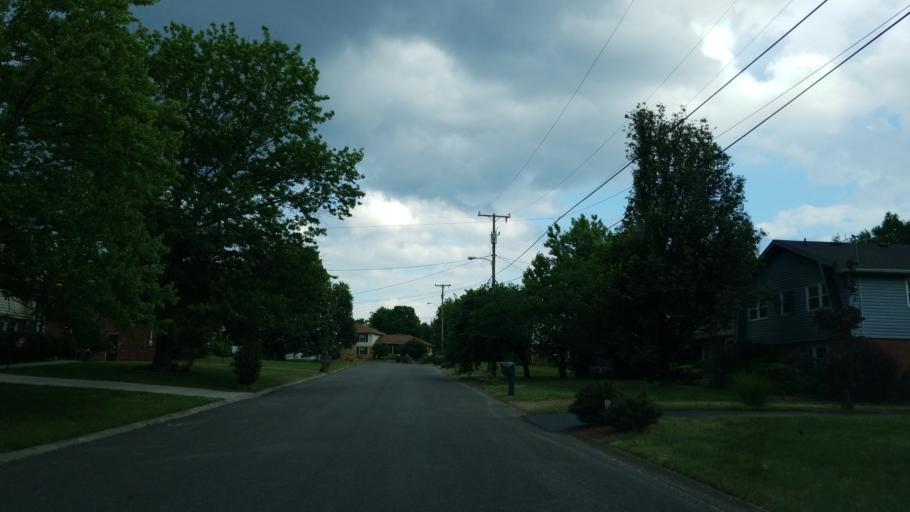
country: US
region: Tennessee
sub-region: Rutherford County
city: La Vergne
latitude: 36.0972
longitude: -86.6085
